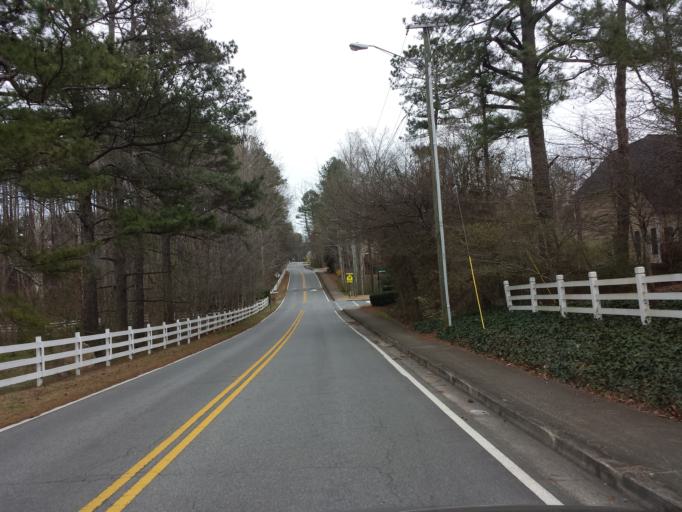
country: US
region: Georgia
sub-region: Cobb County
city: Marietta
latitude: 34.0020
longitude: -84.5143
